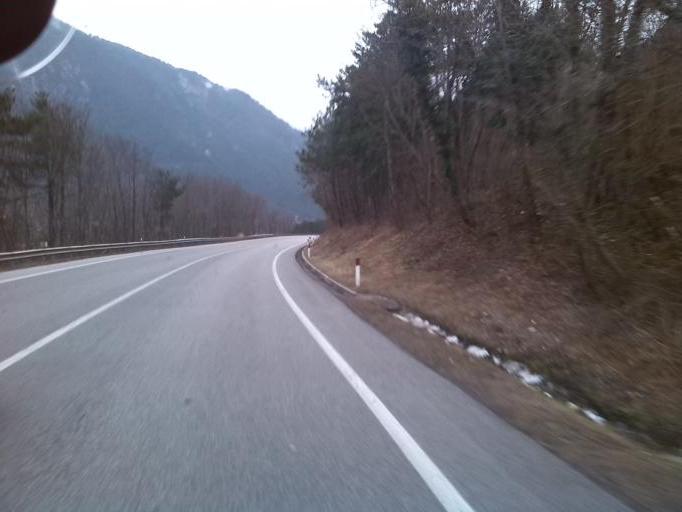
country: IT
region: Friuli Venezia Giulia
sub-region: Provincia di Udine
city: Moggio di Sotto
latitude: 46.3920
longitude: 13.1644
